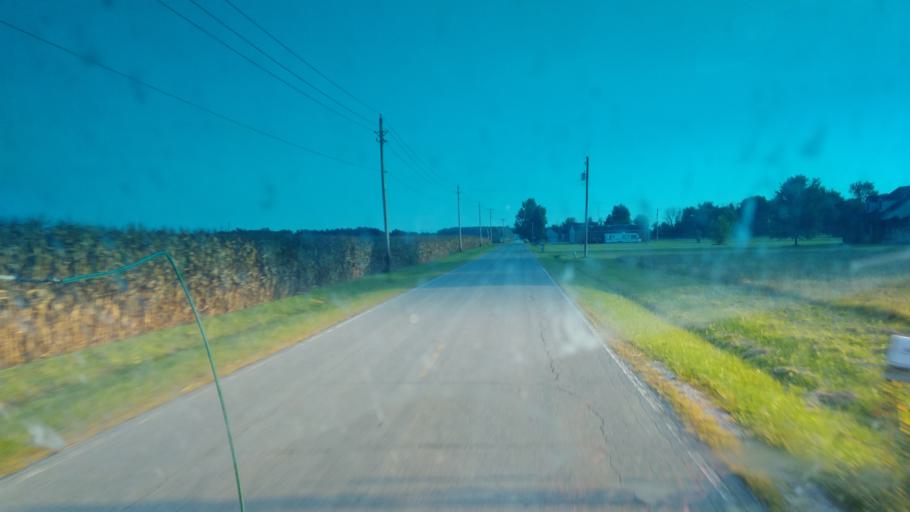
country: US
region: Ohio
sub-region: Crawford County
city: Galion
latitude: 40.8093
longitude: -82.8189
